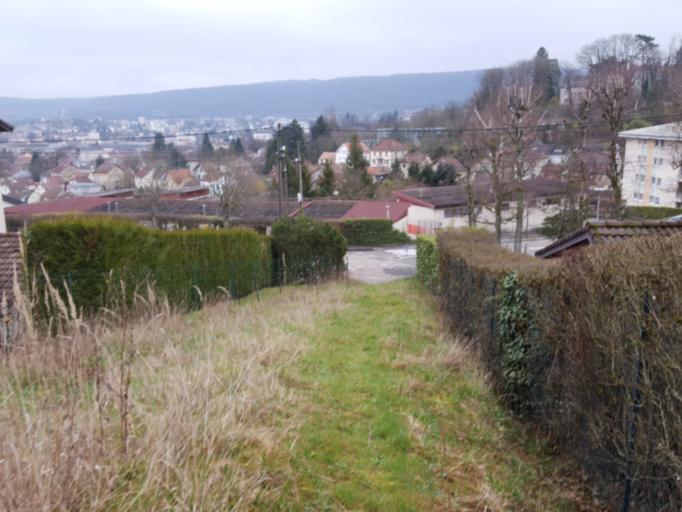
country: FR
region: Franche-Comte
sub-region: Departement du Jura
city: Lons-le-Saunier
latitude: 46.6649
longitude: 5.5408
